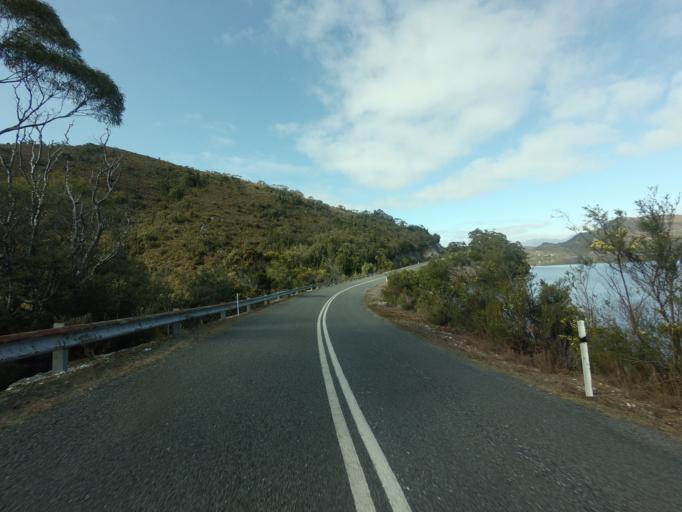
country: AU
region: Tasmania
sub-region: Huon Valley
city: Geeveston
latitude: -42.8298
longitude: 146.1263
